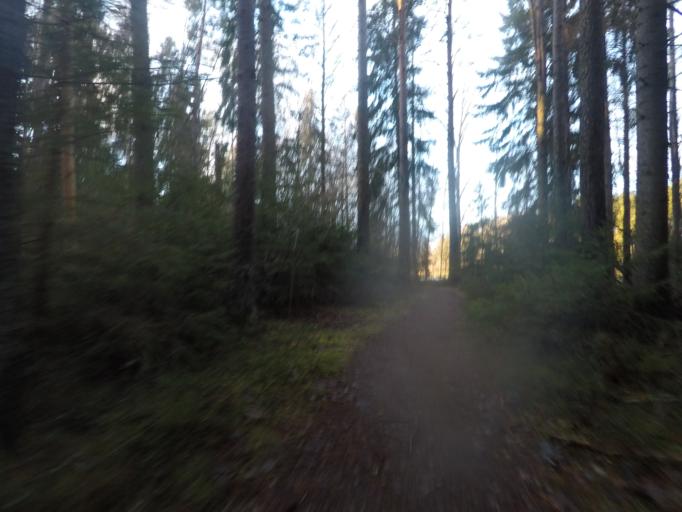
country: SE
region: Soedermanland
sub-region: Eskilstuna Kommun
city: Eskilstuna
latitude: 59.3936
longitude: 16.5234
